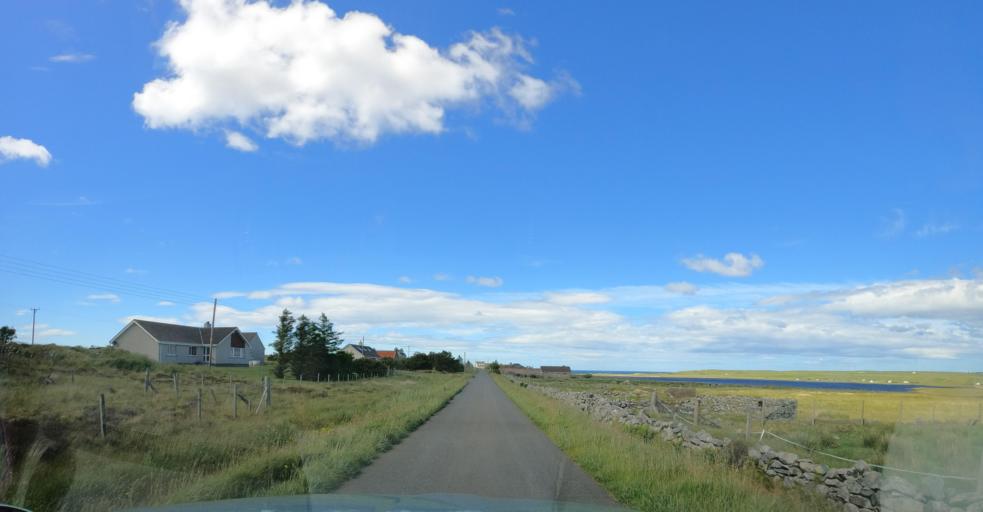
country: GB
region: Scotland
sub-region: Eilean Siar
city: Isle of Lewis
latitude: 58.3491
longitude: -6.5454
